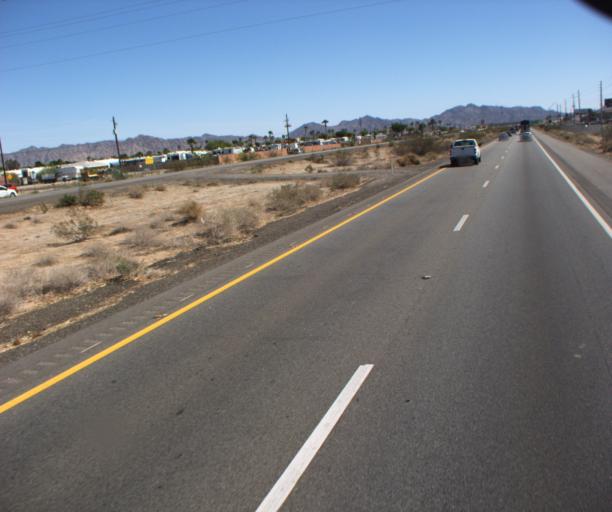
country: US
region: Arizona
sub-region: Yuma County
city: Fortuna Foothills
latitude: 32.6704
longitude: -114.4562
